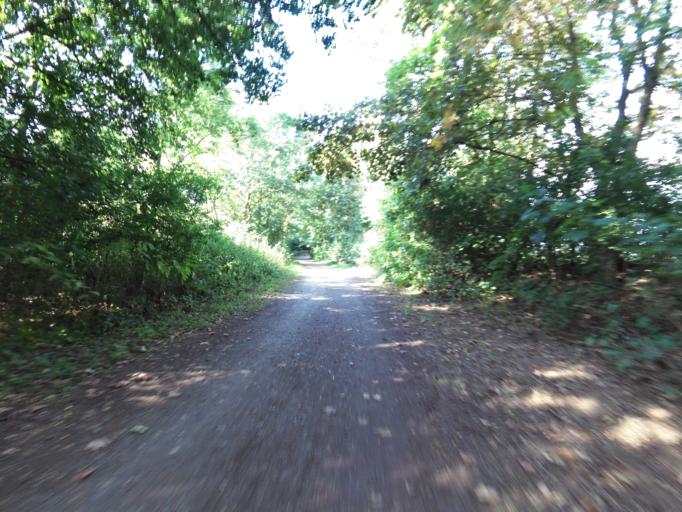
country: DE
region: North Rhine-Westphalia
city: Huckelhoven
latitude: 51.0309
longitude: 6.2332
